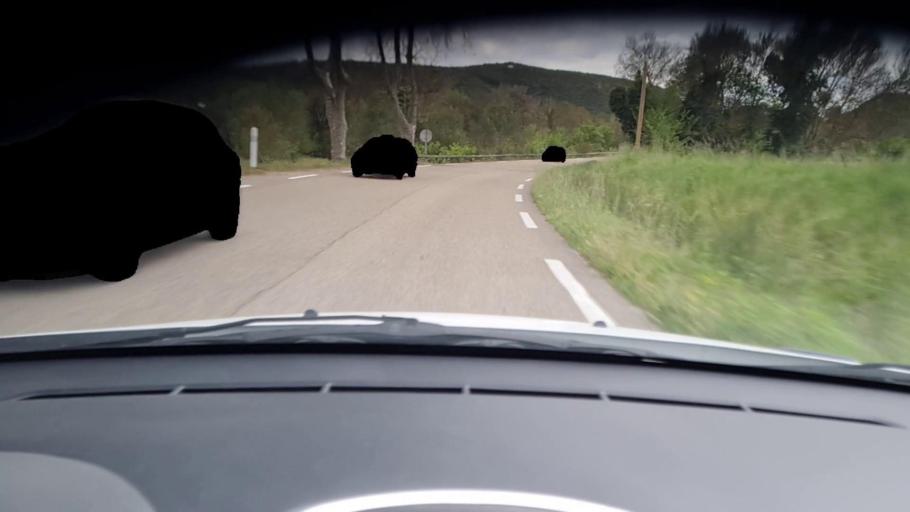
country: FR
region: Languedoc-Roussillon
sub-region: Departement du Gard
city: Blauzac
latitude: 43.9464
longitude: 4.3791
